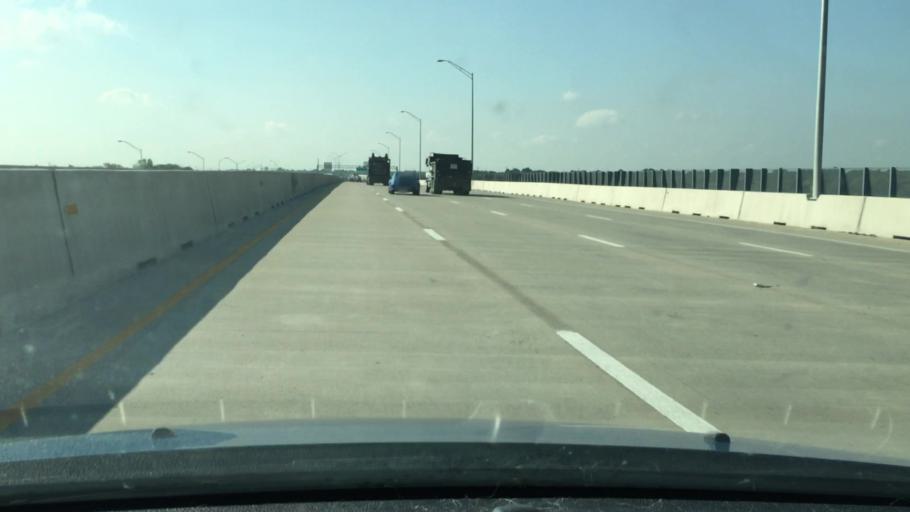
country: US
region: Texas
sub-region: Denton County
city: Lake Dallas
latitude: 33.1022
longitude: -97.0284
